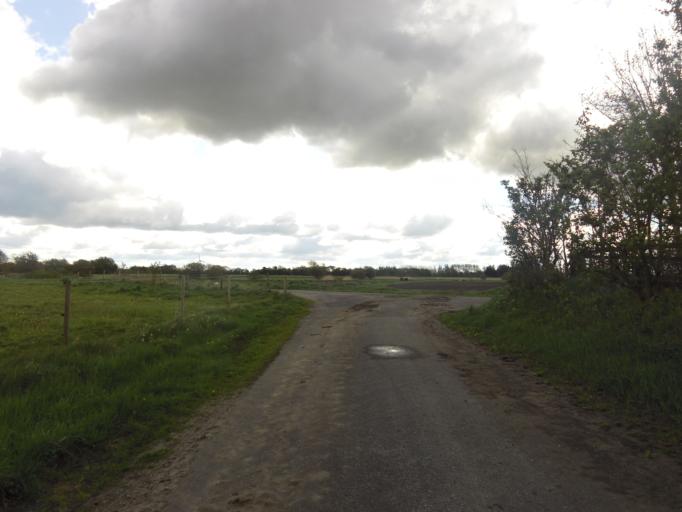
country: DK
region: South Denmark
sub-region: Tonder Kommune
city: Logumkloster
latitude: 55.1153
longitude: 8.9575
